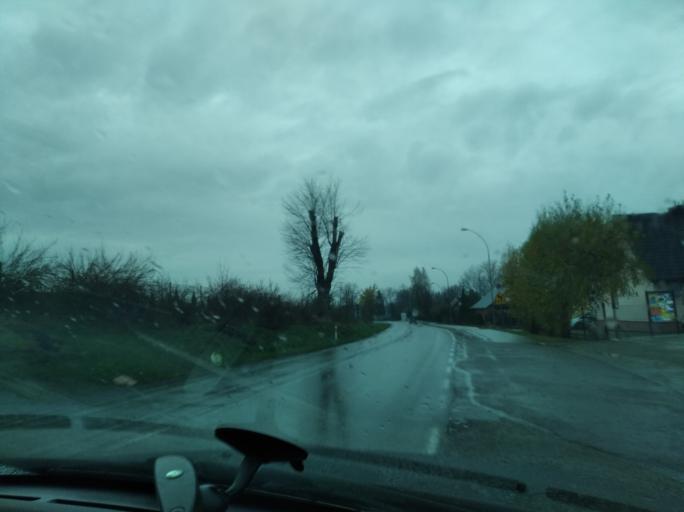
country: PL
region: Subcarpathian Voivodeship
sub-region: Powiat lancucki
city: Albigowa
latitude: 50.0298
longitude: 22.2281
